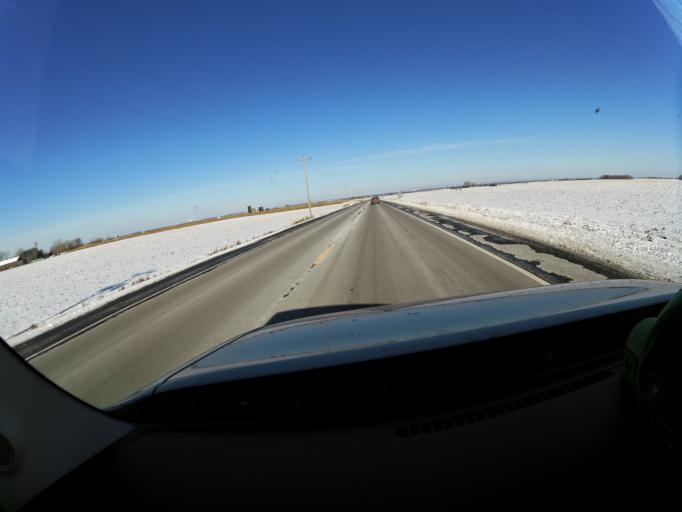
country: US
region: Minnesota
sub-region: Dakota County
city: Hastings
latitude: 44.6687
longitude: -92.9316
